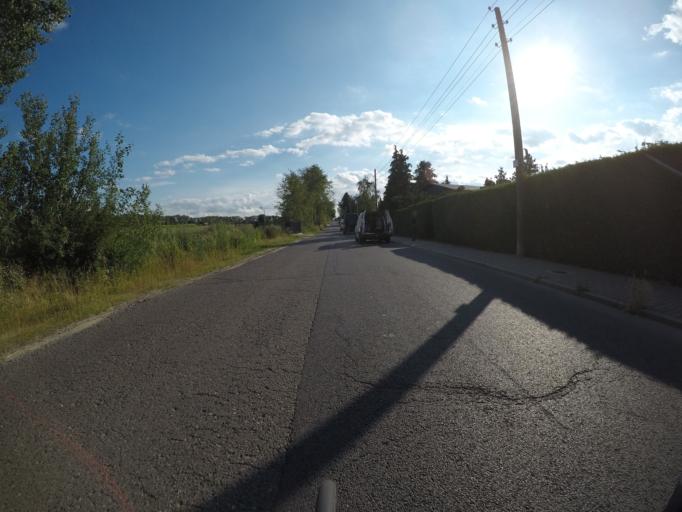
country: DE
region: Berlin
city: Falkenberg
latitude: 52.5875
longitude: 13.5380
